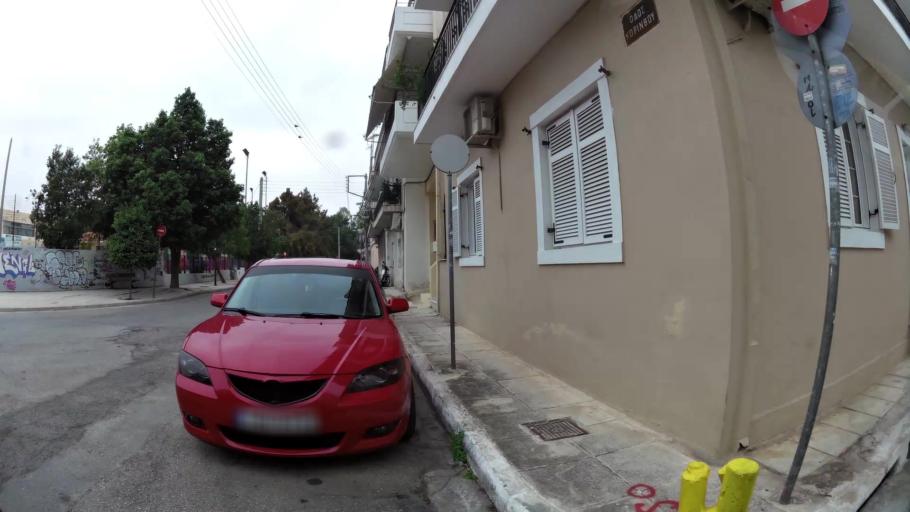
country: GR
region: Attica
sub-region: Nomarchia Athinas
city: Aigaleo
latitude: 37.9968
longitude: 23.6757
